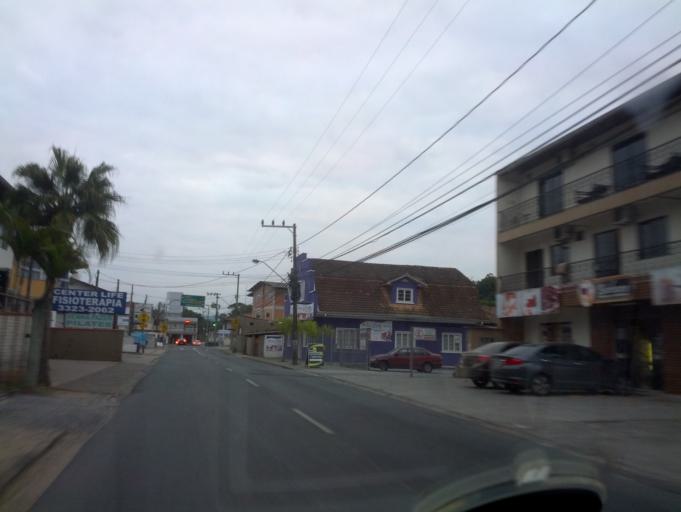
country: BR
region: Santa Catarina
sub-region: Blumenau
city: Blumenau
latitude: -26.8726
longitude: -49.0873
